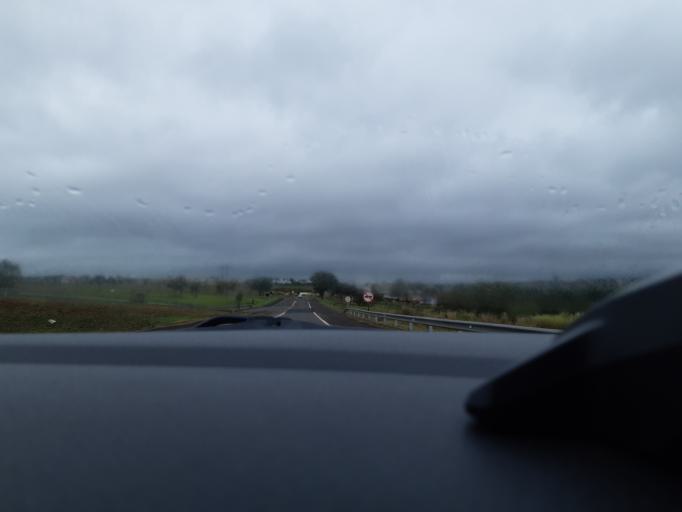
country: BR
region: Sao Paulo
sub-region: Ourinhos
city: Ourinhos
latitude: -22.9765
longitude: -49.9024
